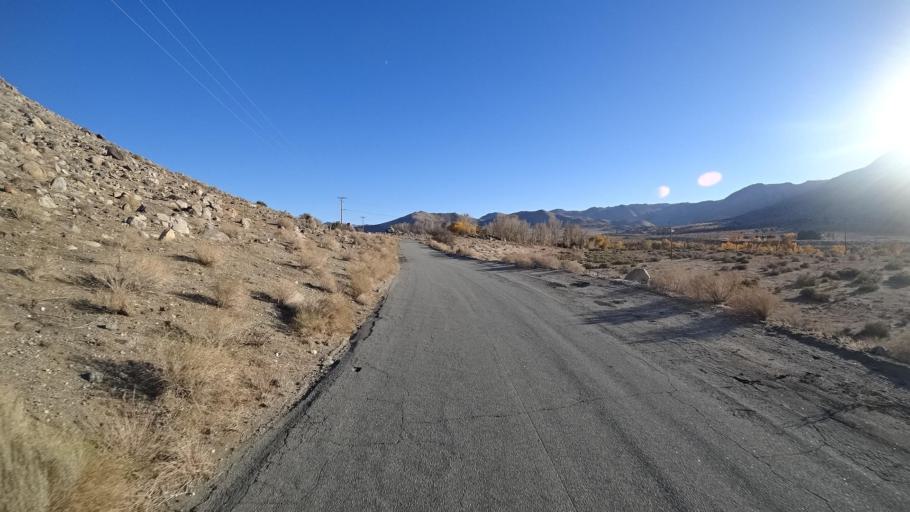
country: US
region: California
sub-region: Kern County
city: Weldon
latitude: 35.5670
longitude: -118.2474
